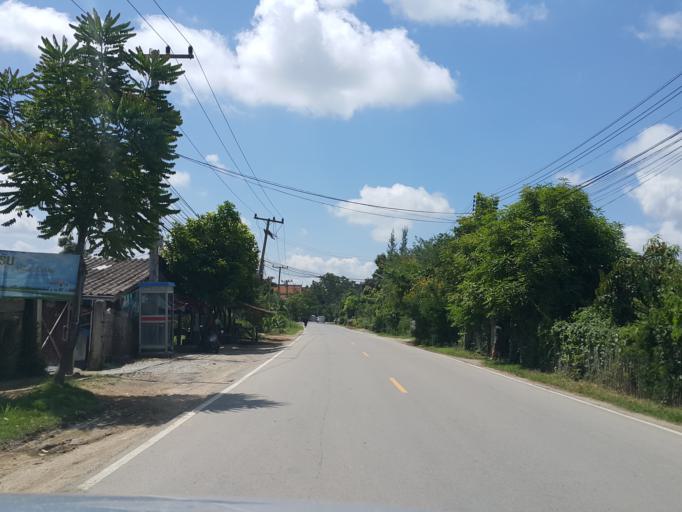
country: TH
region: Chiang Mai
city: San Kamphaeng
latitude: 18.7019
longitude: 99.1047
